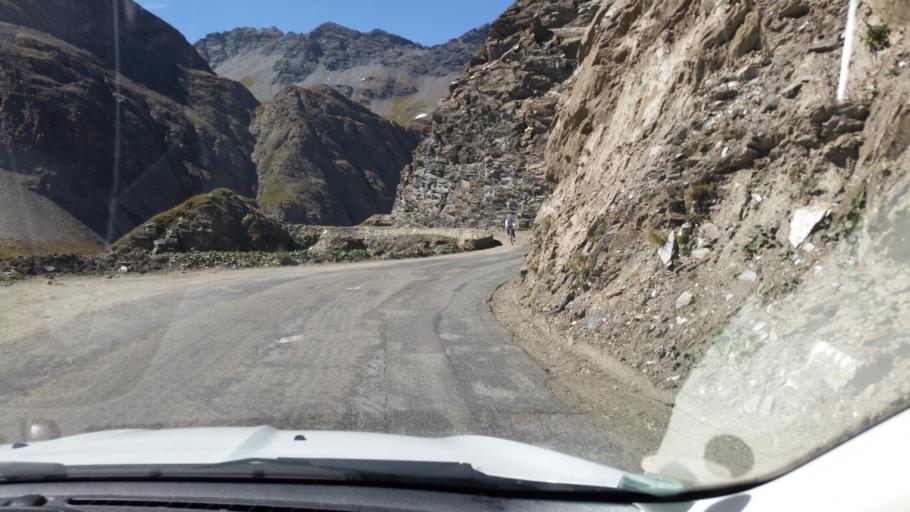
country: FR
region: Rhone-Alpes
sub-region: Departement de la Savoie
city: Val-d'Isere
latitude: 45.4008
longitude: 7.0400
